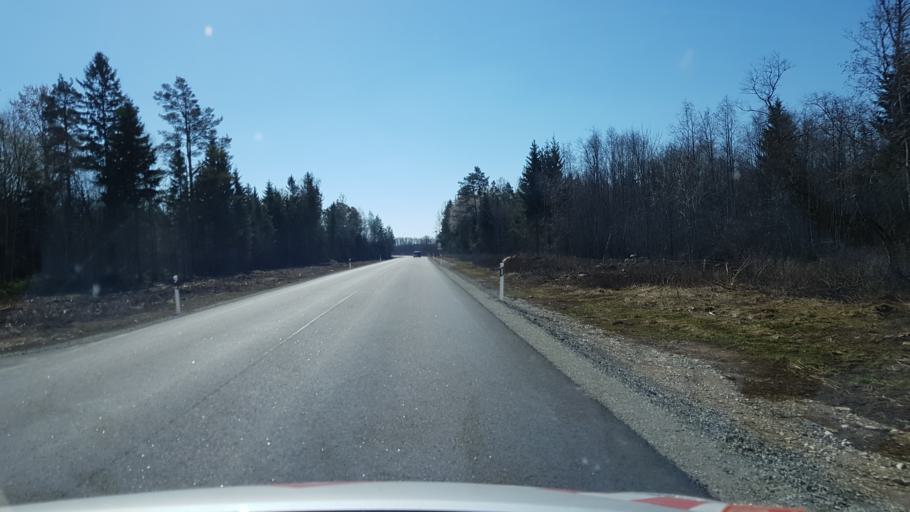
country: EE
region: Laeaene-Virumaa
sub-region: Vinni vald
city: Vinni
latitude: 59.0675
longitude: 26.6377
